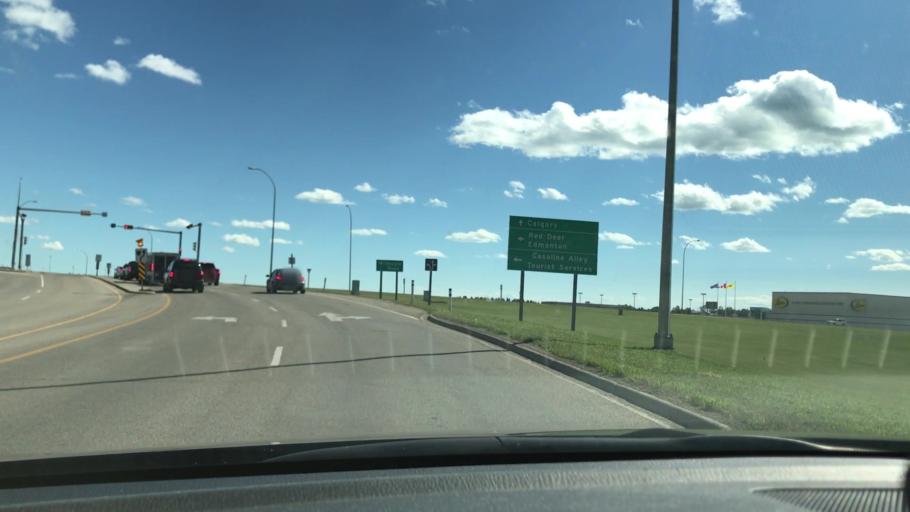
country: CA
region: Alberta
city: Red Deer
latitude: 52.2024
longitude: -113.8172
